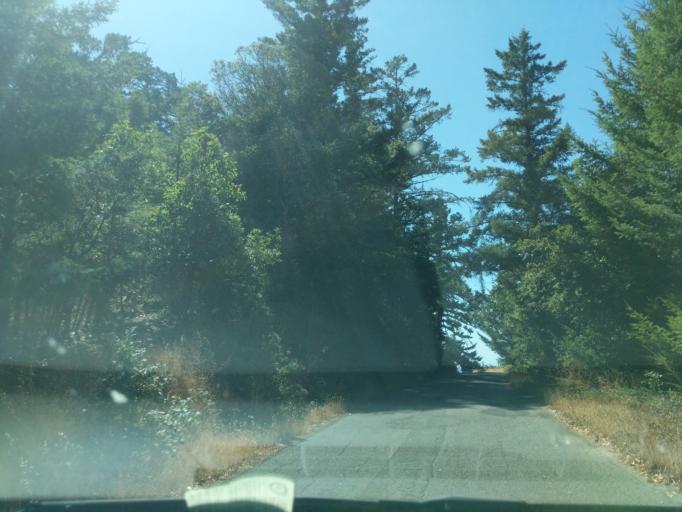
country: US
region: California
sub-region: Sonoma County
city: Monte Rio
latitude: 38.5321
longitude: -123.2237
